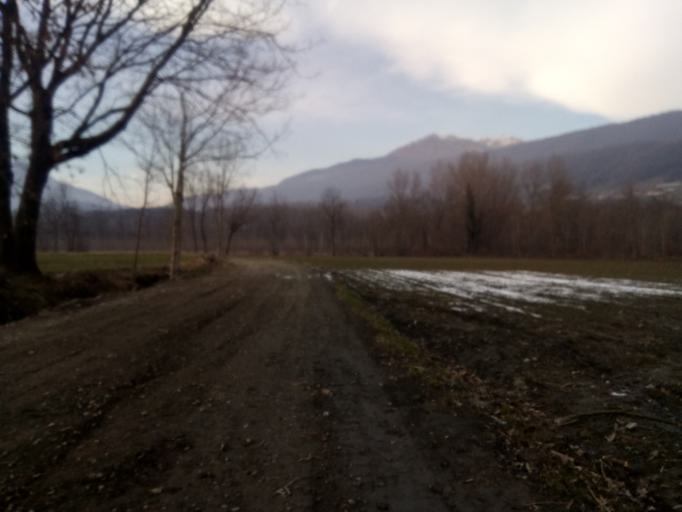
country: IT
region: Piedmont
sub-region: Provincia di Torino
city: Burolo
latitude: 45.4843
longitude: 7.9210
